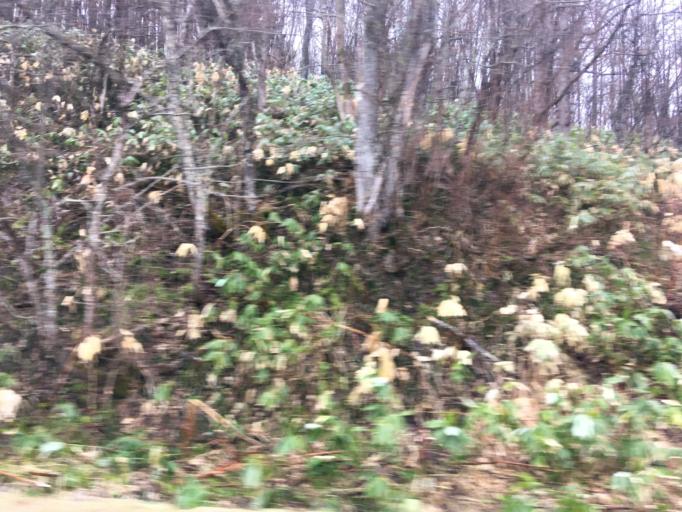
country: JP
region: Hokkaido
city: Nayoro
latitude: 44.0782
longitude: 142.4188
